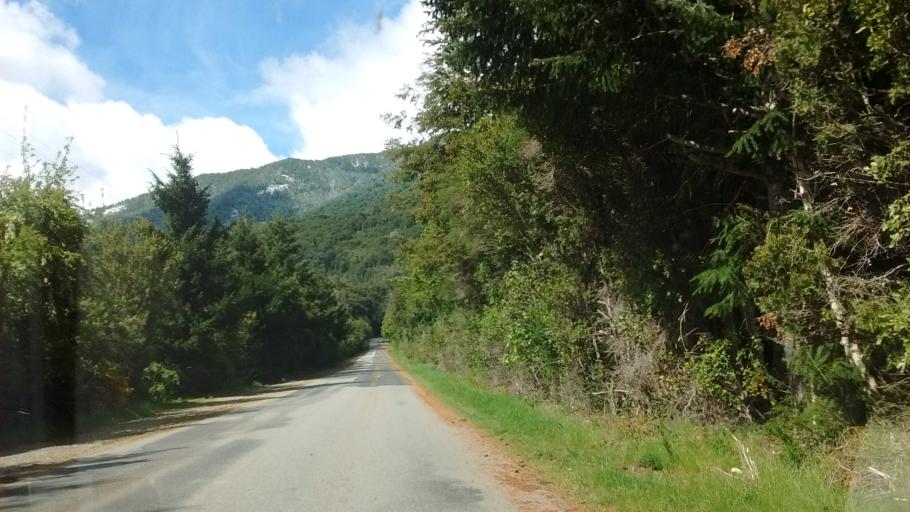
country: AR
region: Rio Negro
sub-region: Departamento de Bariloche
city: San Carlos de Bariloche
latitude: -41.0800
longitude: -71.5450
